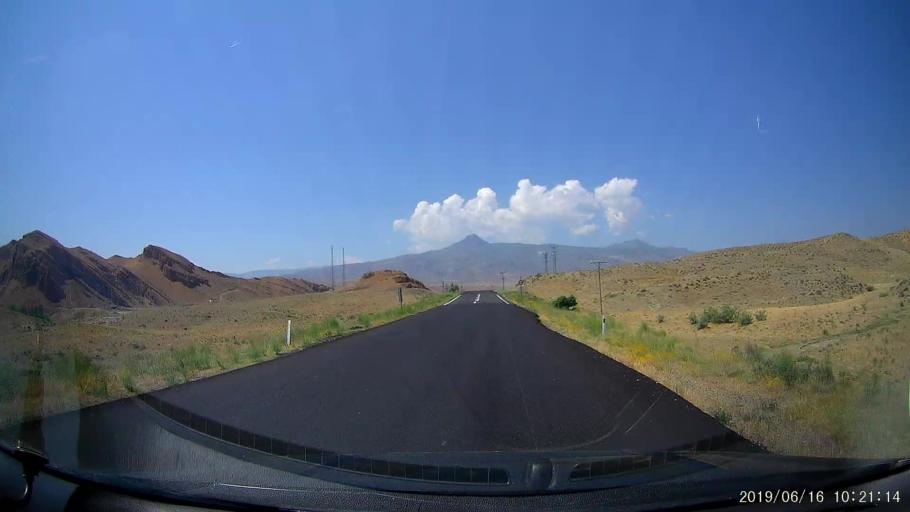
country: TR
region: Igdir
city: Tuzluca
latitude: 40.1395
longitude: 43.6391
